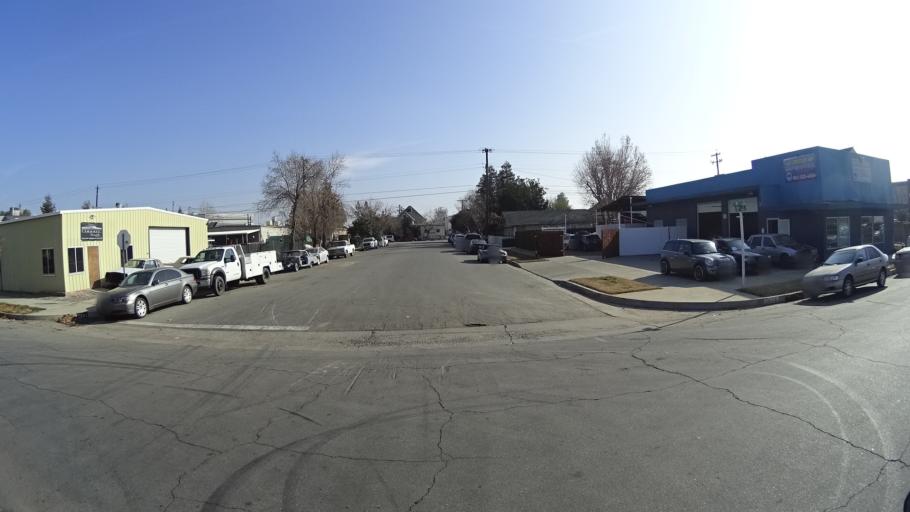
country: US
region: California
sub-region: Kern County
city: Bakersfield
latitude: 35.3819
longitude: -119.0176
